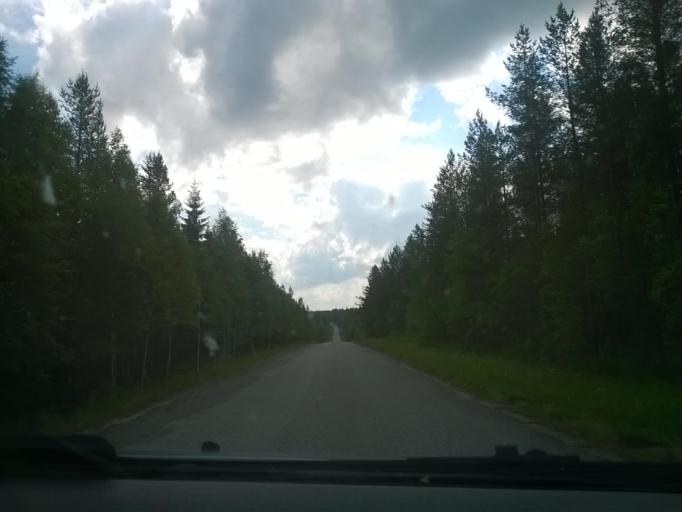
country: FI
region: Kainuu
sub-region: Kehys-Kainuu
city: Kuhmo
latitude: 64.4433
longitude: 29.7015
